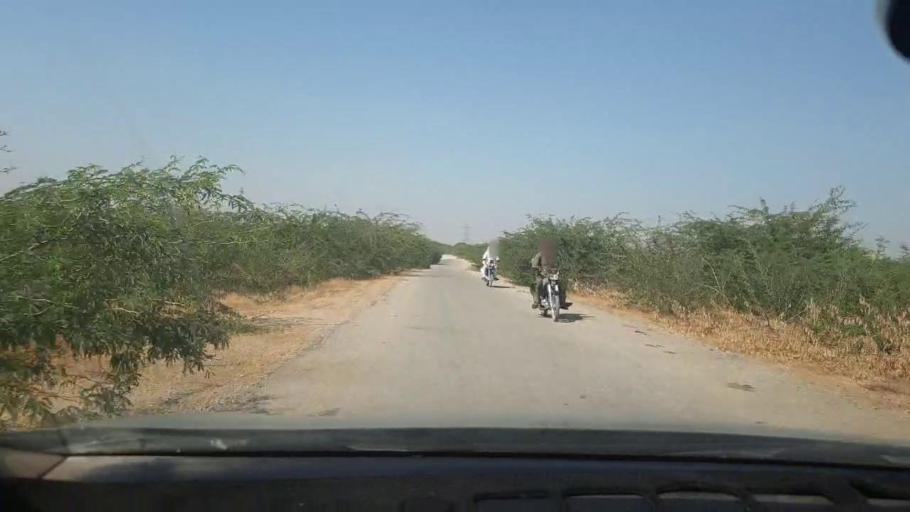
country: PK
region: Sindh
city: Malir Cantonment
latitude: 25.1604
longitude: 67.1626
